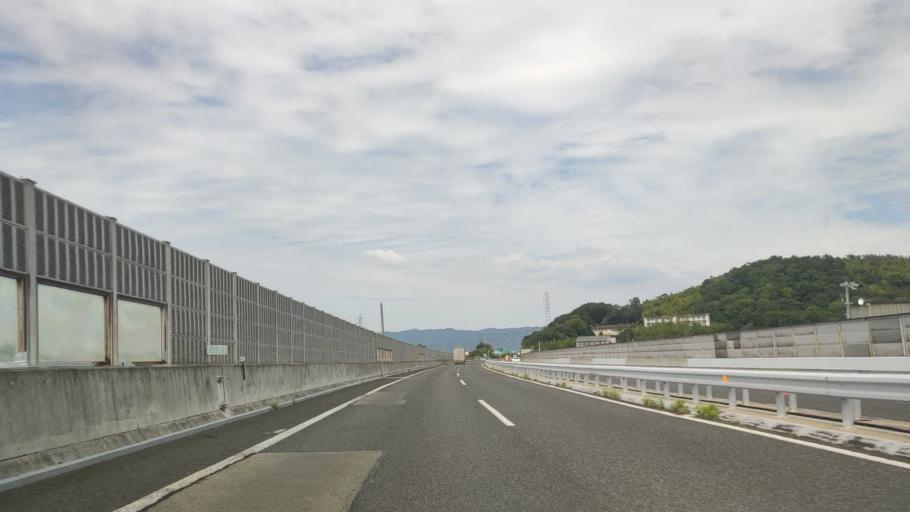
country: JP
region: Wakayama
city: Wakayama-shi
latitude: 34.2264
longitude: 135.2138
